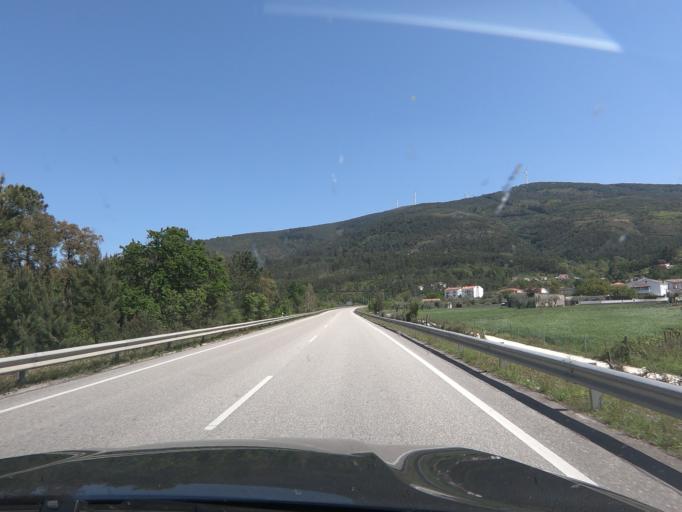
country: PT
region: Coimbra
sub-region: Lousa
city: Lousa
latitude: 40.1237
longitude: -8.2306
